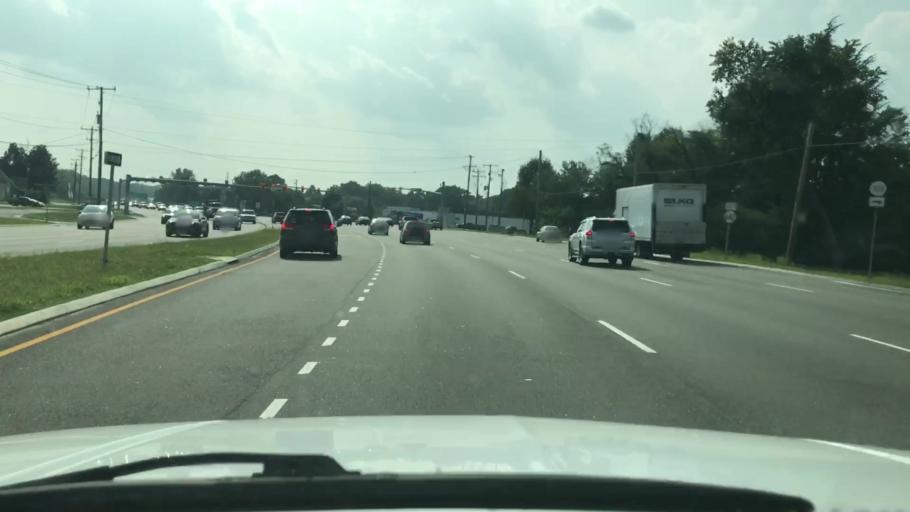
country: US
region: Virginia
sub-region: Hanover County
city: Mechanicsville
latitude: 37.6110
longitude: -77.3512
